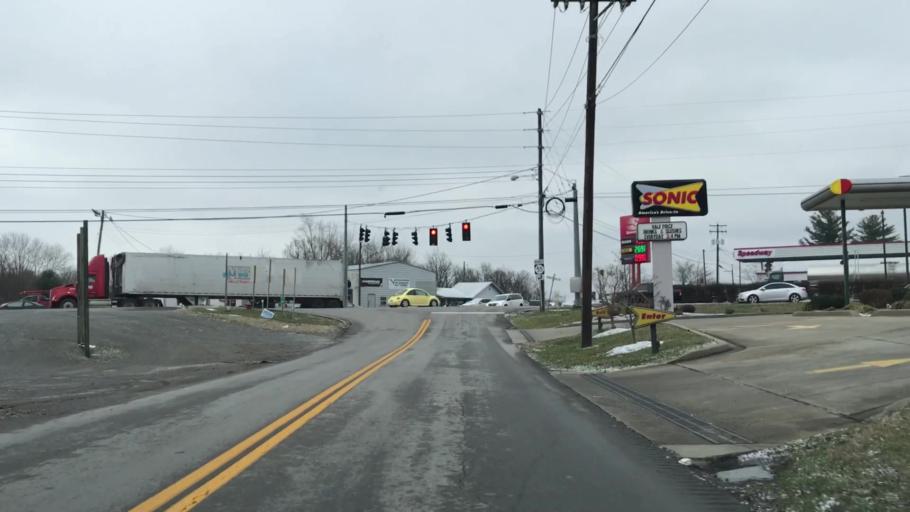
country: US
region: Kentucky
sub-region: Adair County
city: Columbia
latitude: 37.0918
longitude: -85.3051
